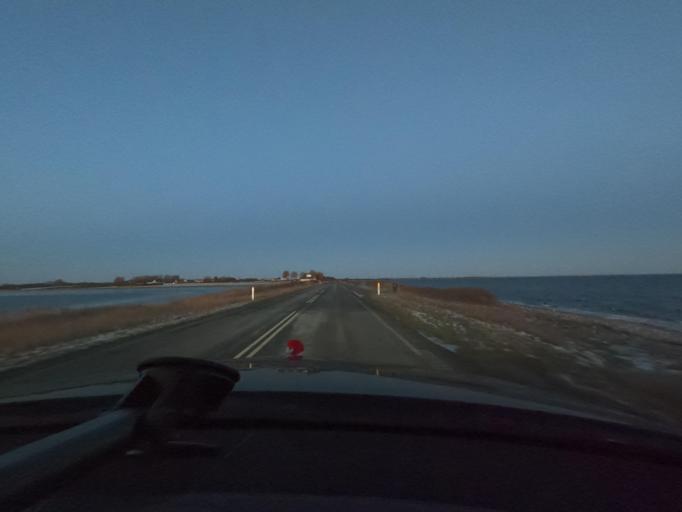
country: DE
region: Schleswig-Holstein
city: Pommerby
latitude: 54.8572
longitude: 9.9952
